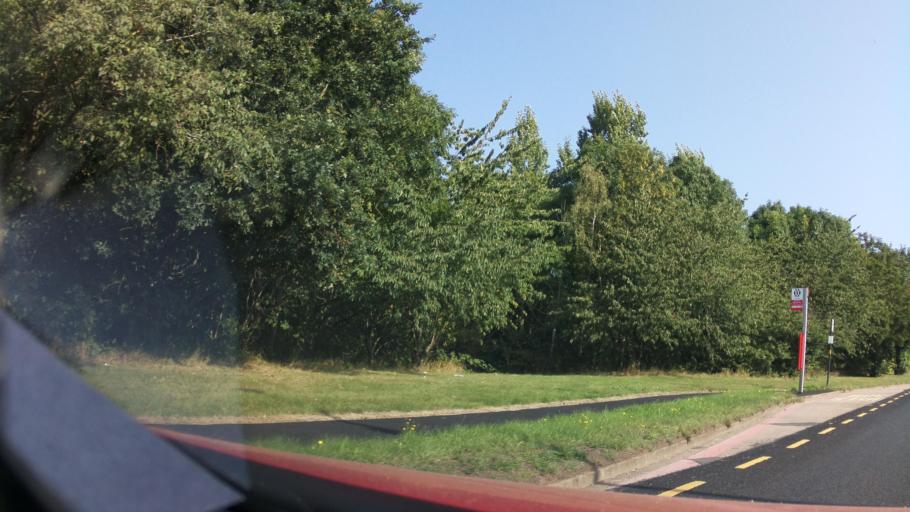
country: GB
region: England
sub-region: Sandwell
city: West Bromwich
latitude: 52.5387
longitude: -1.9655
